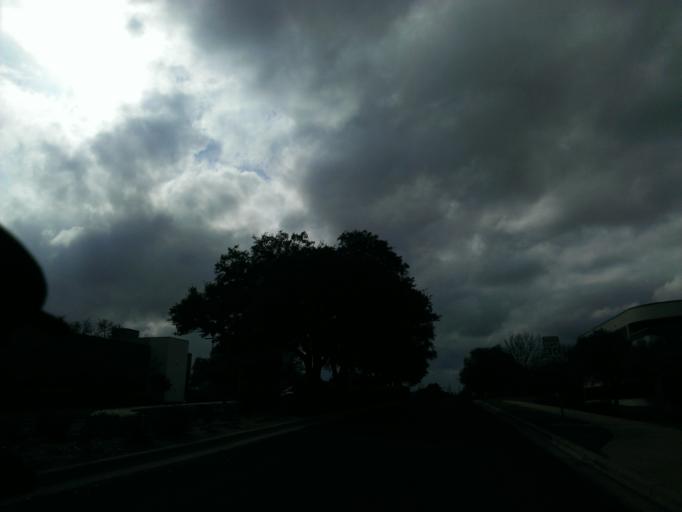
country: US
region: Texas
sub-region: Travis County
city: Wells Branch
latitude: 30.3933
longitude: -97.6720
